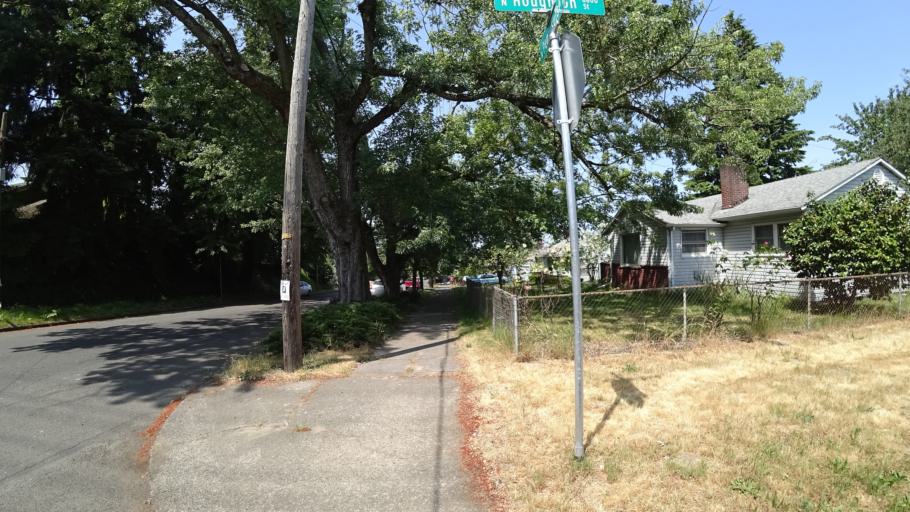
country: US
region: Washington
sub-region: Clark County
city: Vancouver
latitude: 45.5870
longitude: -122.6971
